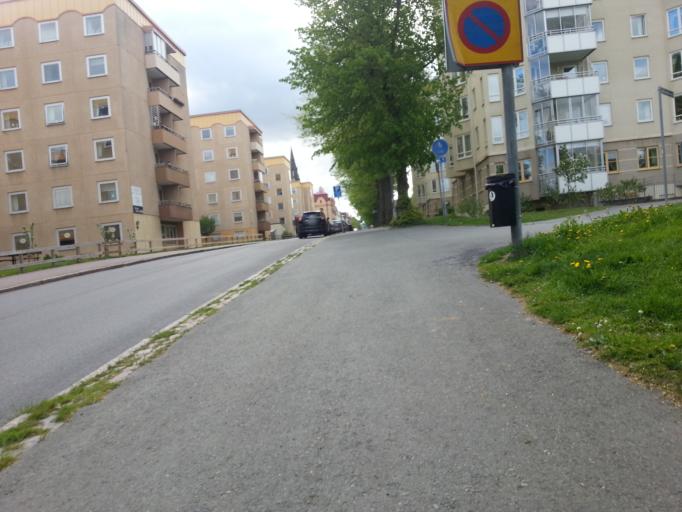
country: SE
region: Joenkoeping
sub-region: Jonkopings Kommun
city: Jonkoping
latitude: 57.7827
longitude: 14.1533
